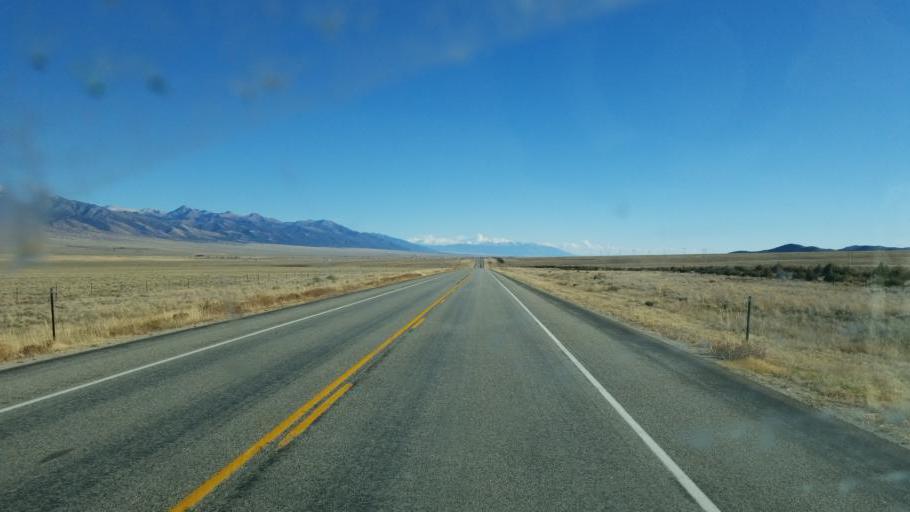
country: US
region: Colorado
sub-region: Chaffee County
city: Salida
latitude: 38.2890
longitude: -105.9807
